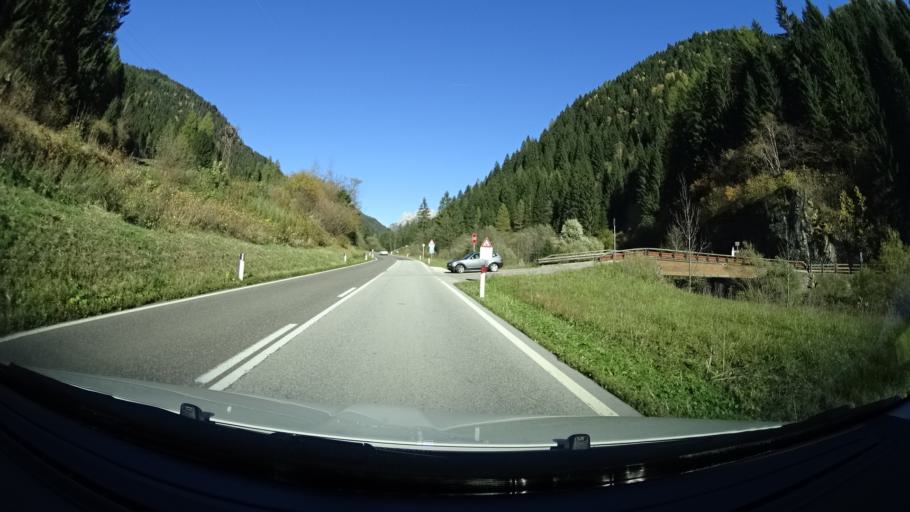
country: IT
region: Trentino-Alto Adige
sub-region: Provincia di Trento
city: Predazzo
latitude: 46.3314
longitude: 11.6030
